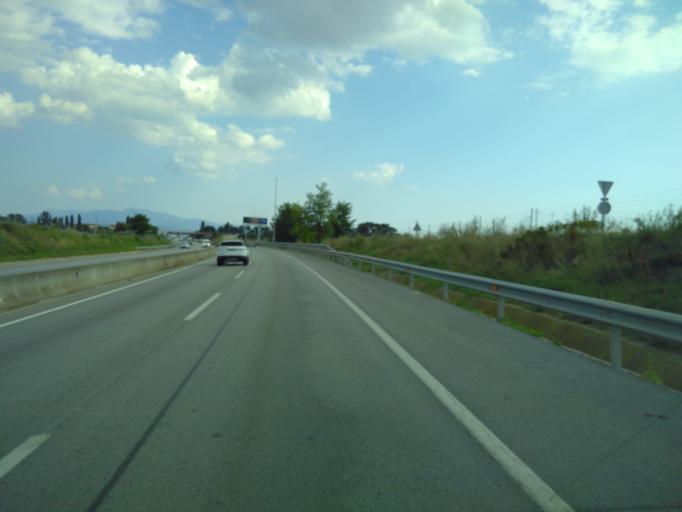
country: ES
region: Catalonia
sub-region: Provincia de Barcelona
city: Santa Cecilia de Voltrega
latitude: 41.9793
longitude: 2.2405
